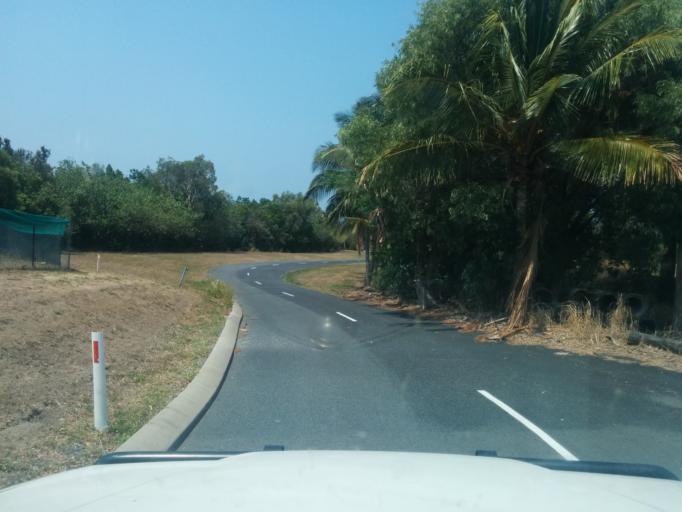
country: AU
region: Queensland
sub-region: Cairns
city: Redlynch
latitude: -16.8729
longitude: 145.7352
